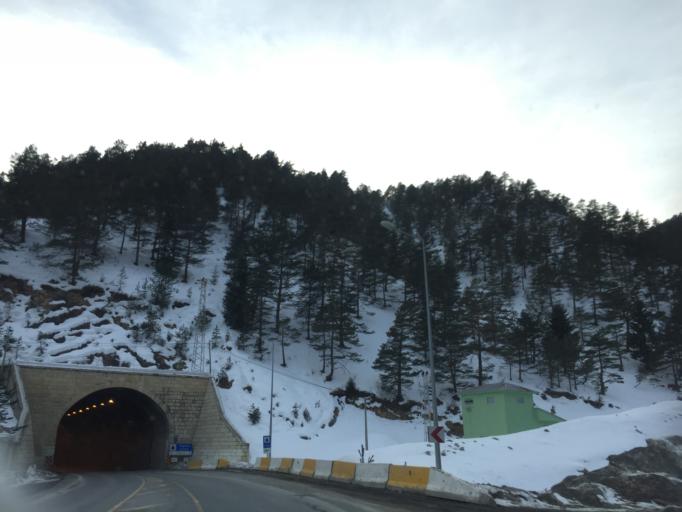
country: TR
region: Gumushane
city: Torul
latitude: 40.6561
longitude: 39.4007
